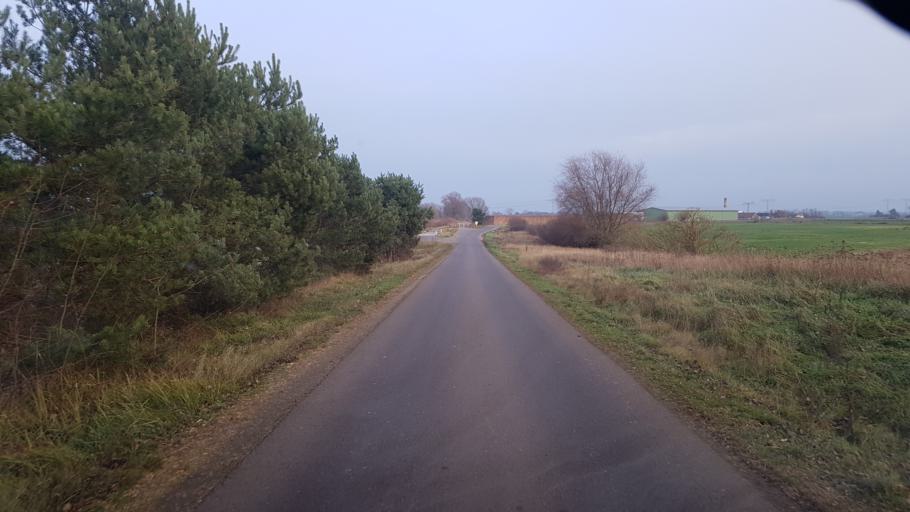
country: DE
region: Brandenburg
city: Wiesenau
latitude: 52.2389
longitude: 14.5935
